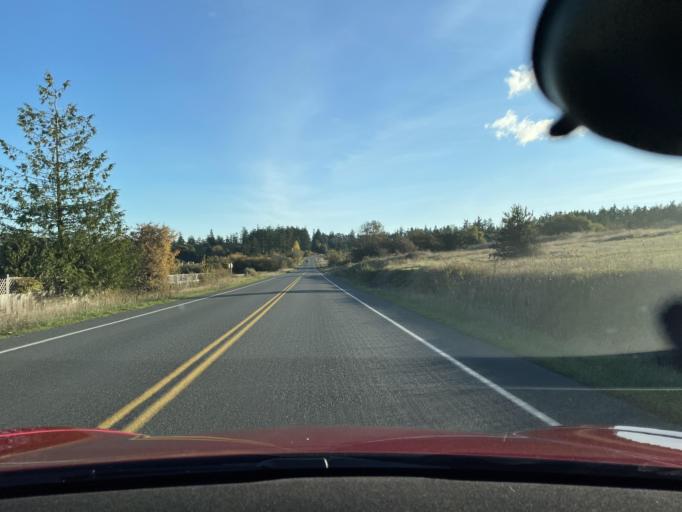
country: US
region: Washington
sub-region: San Juan County
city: Friday Harbor
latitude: 48.5160
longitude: -123.0231
